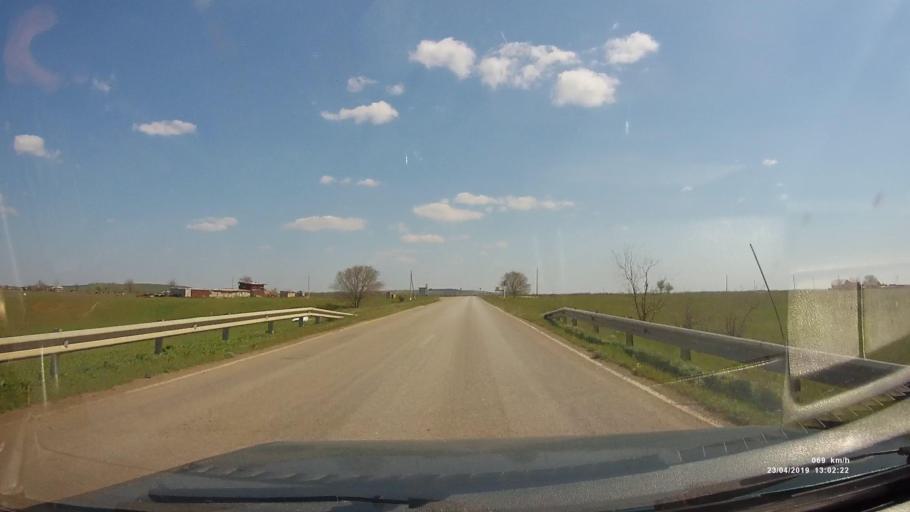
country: RU
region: Kalmykiya
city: Yashalta
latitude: 46.6008
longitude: 42.6684
